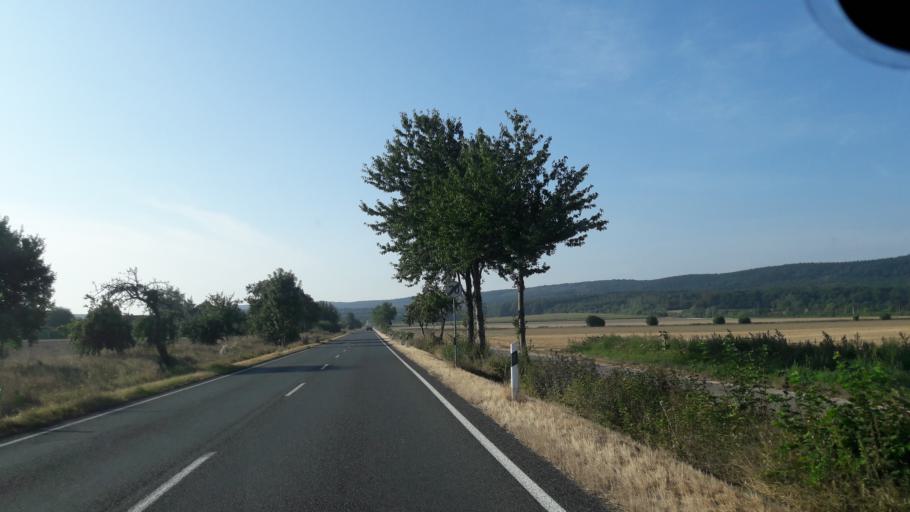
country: DE
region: Lower Saxony
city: Giesen
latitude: 52.1476
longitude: 9.8716
